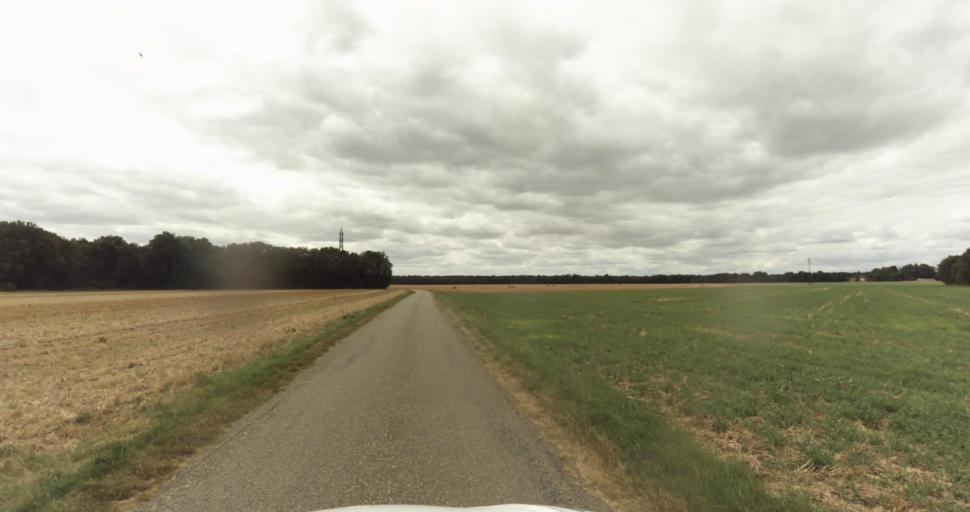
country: FR
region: Haute-Normandie
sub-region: Departement de l'Eure
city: Saint-Germain-sur-Avre
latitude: 48.7990
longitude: 1.2584
